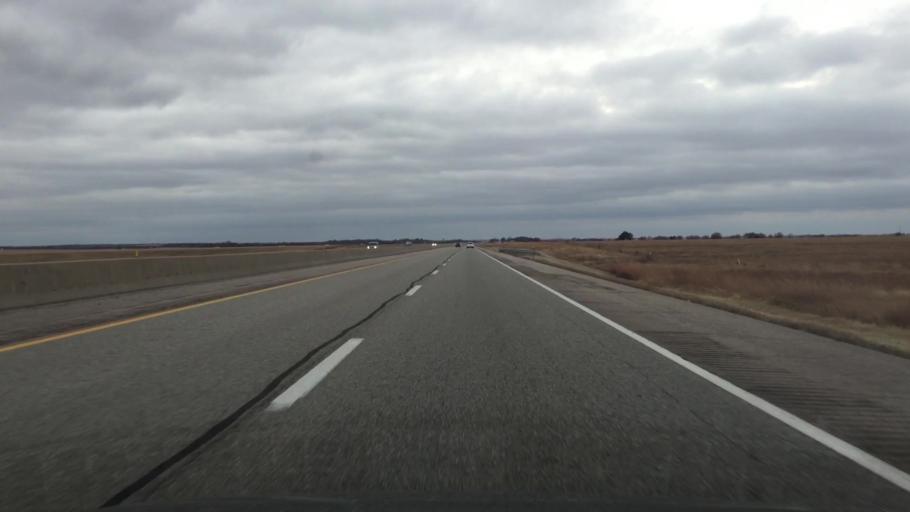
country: US
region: Kansas
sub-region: Butler County
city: El Dorado
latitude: 37.9057
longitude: -96.8222
